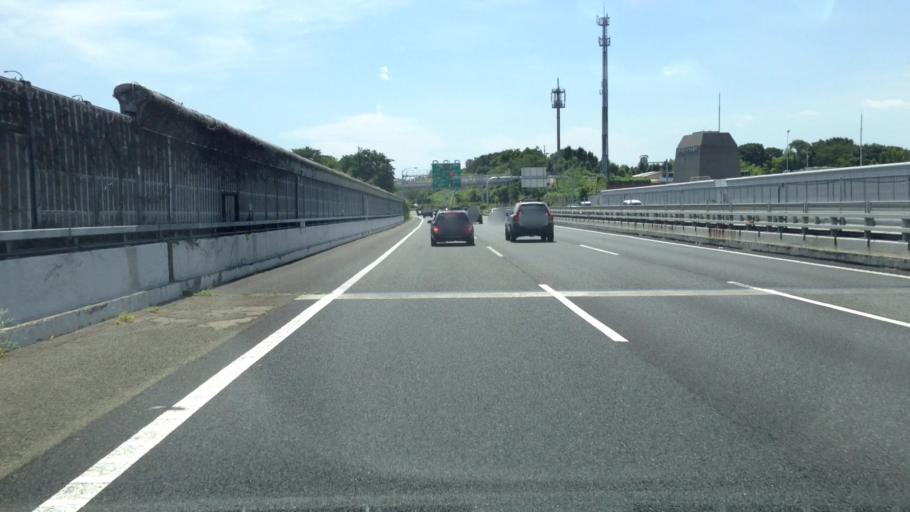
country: JP
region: Kanagawa
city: Yokohama
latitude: 35.5016
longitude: 139.5921
